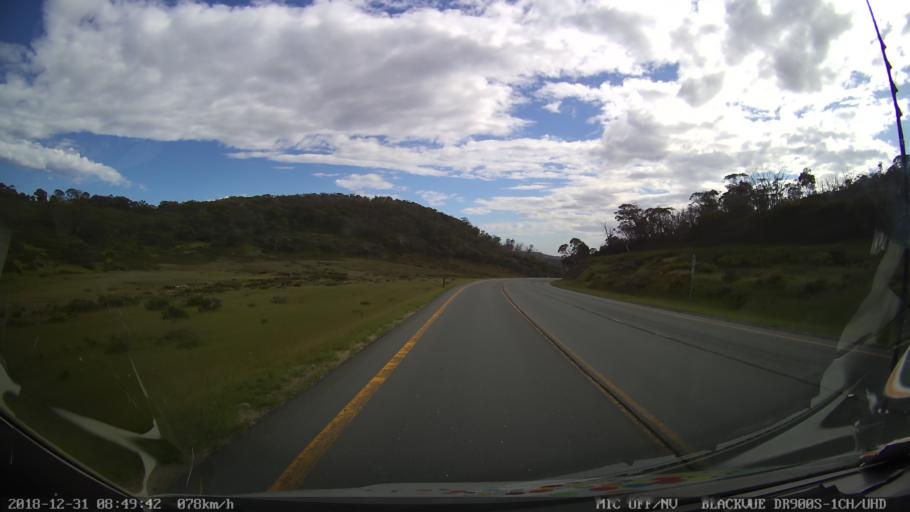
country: AU
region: New South Wales
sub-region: Snowy River
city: Jindabyne
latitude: -36.3594
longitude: 148.5098
